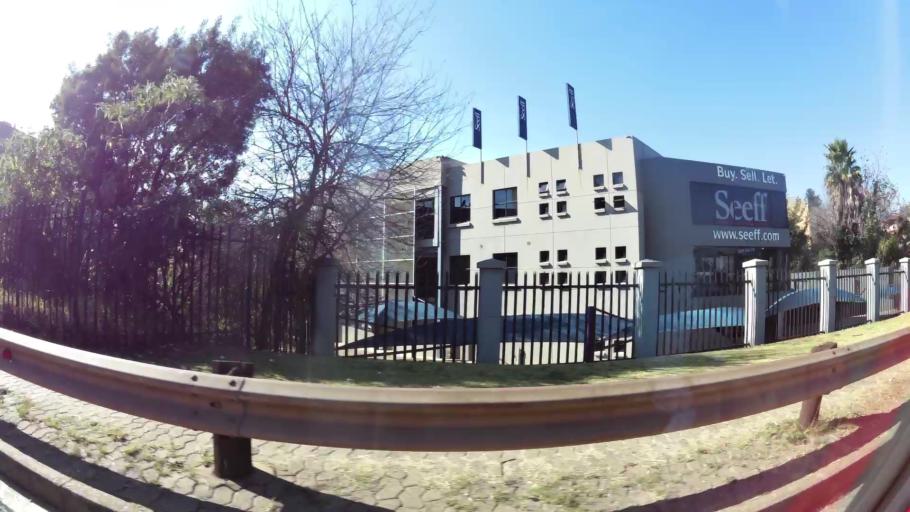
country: ZA
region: Gauteng
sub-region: City of Johannesburg Metropolitan Municipality
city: Roodepoort
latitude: -26.1210
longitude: 27.9601
